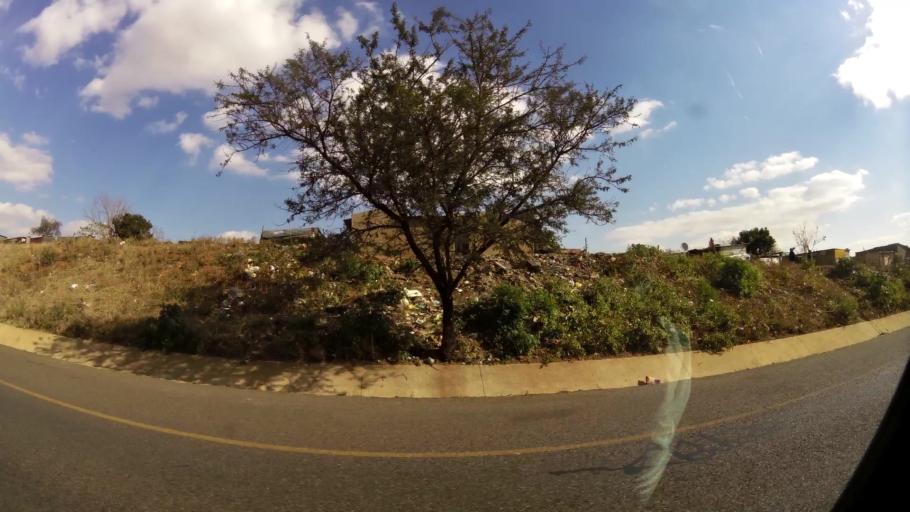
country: ZA
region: Gauteng
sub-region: Ekurhuleni Metropolitan Municipality
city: Tembisa
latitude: -25.9680
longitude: 28.2189
